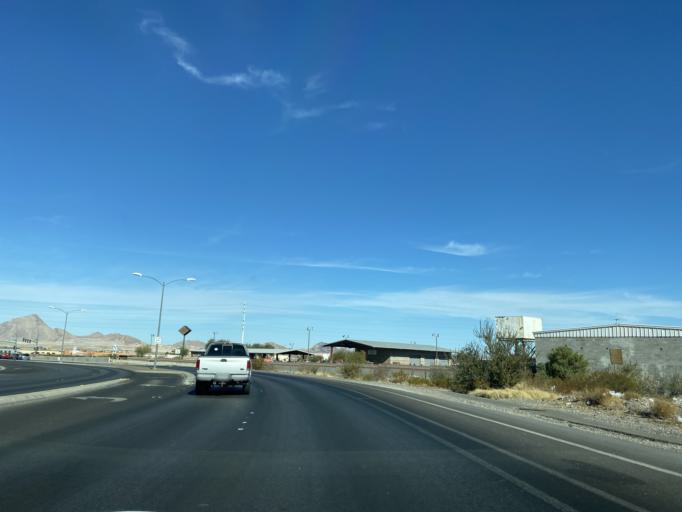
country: US
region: Nevada
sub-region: Clark County
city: Henderson
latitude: 36.0617
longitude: -115.0275
